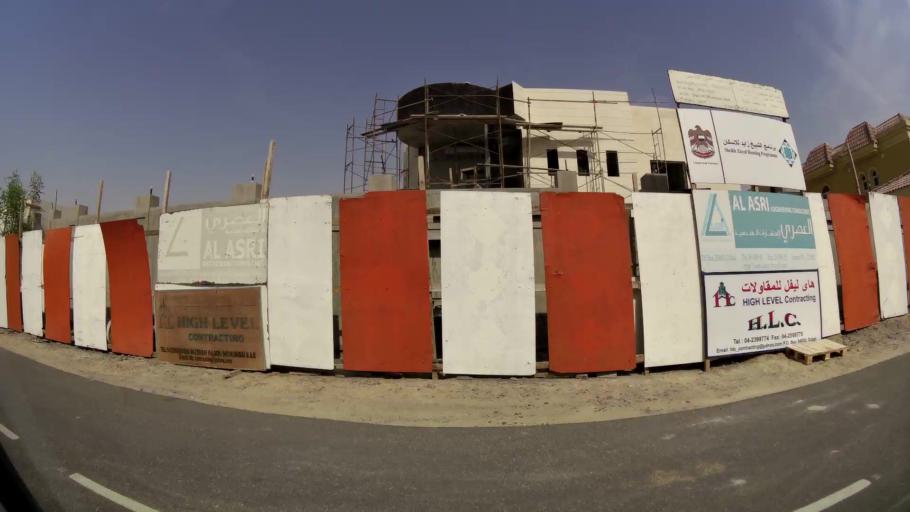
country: AE
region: Ash Shariqah
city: Sharjah
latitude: 25.2681
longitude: 55.4681
